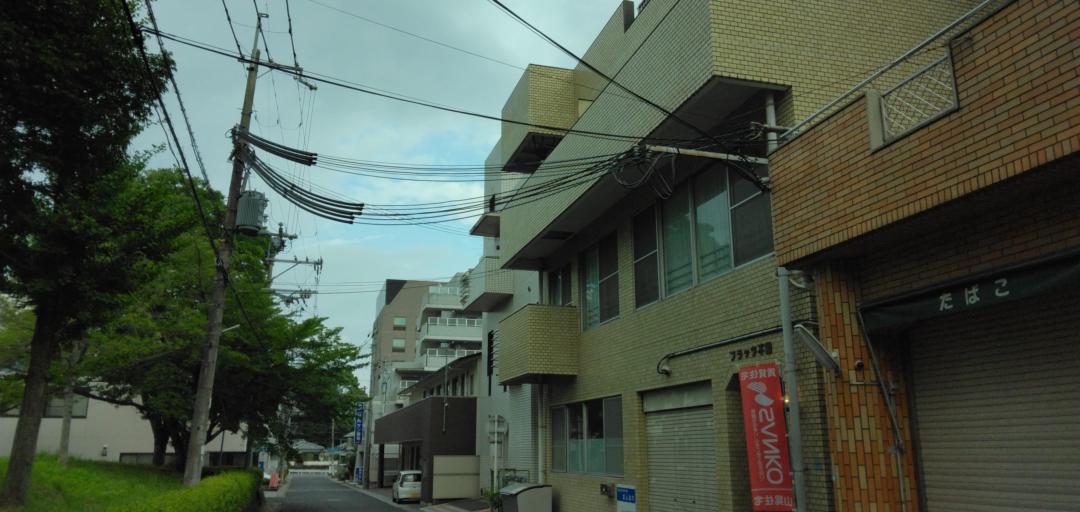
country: JP
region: Osaka
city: Kashihara
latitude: 34.5895
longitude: 135.6864
